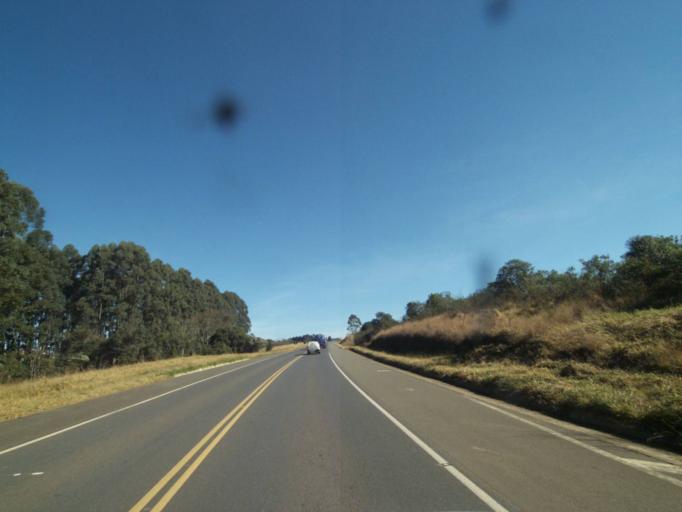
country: BR
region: Parana
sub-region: Tibagi
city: Tibagi
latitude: -24.5231
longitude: -50.4402
